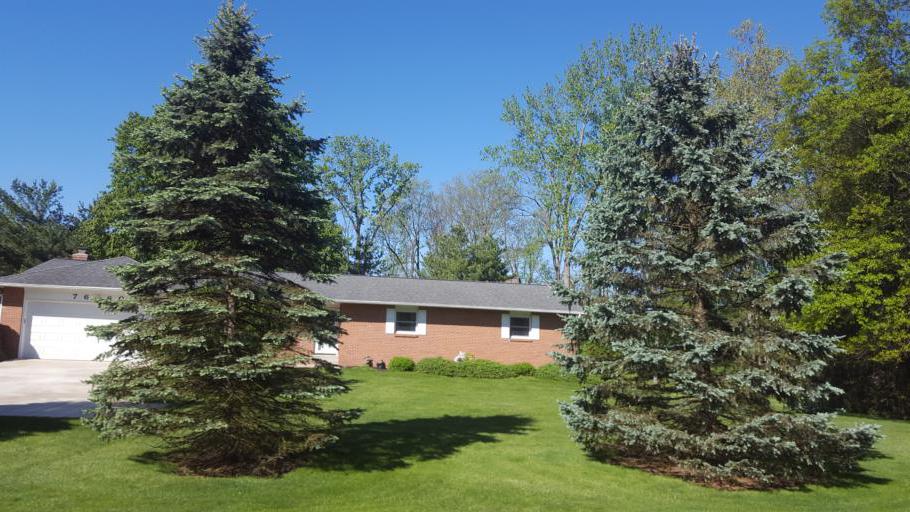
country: US
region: Ohio
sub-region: Franklin County
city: Westerville
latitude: 40.1519
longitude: -82.9420
